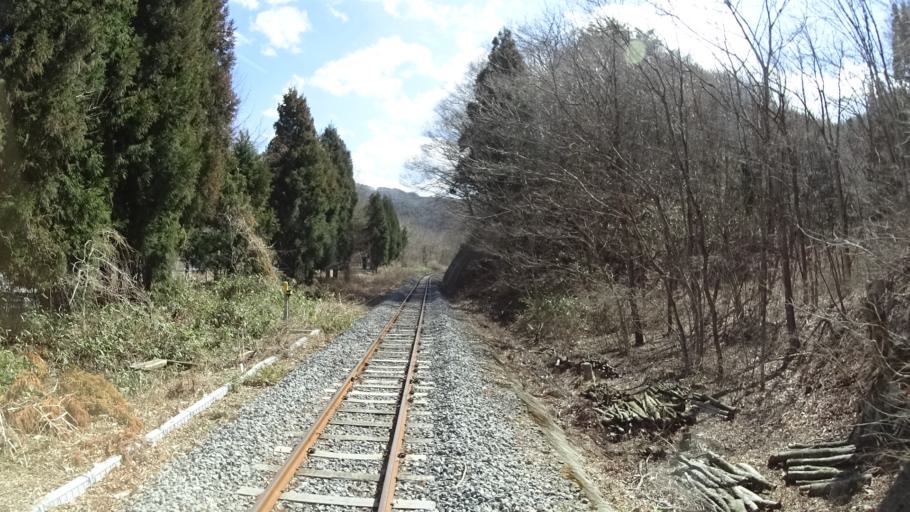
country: JP
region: Iwate
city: Miyako
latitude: 39.5577
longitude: 141.9391
